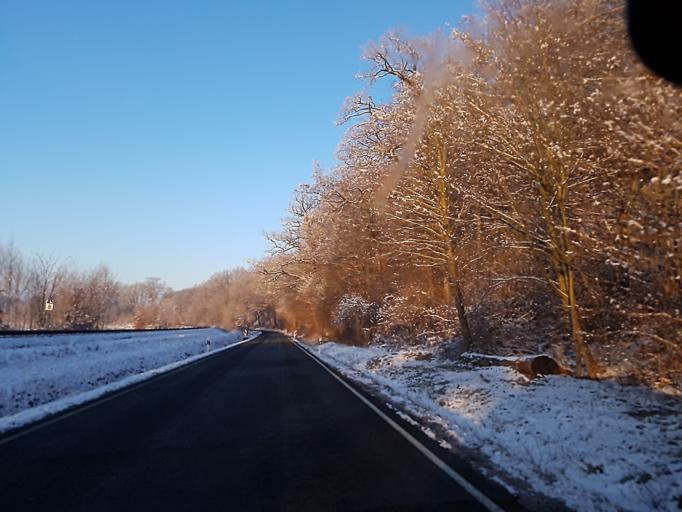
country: DE
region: Saxony
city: Grossweitzschen
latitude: 51.1586
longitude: 12.9977
